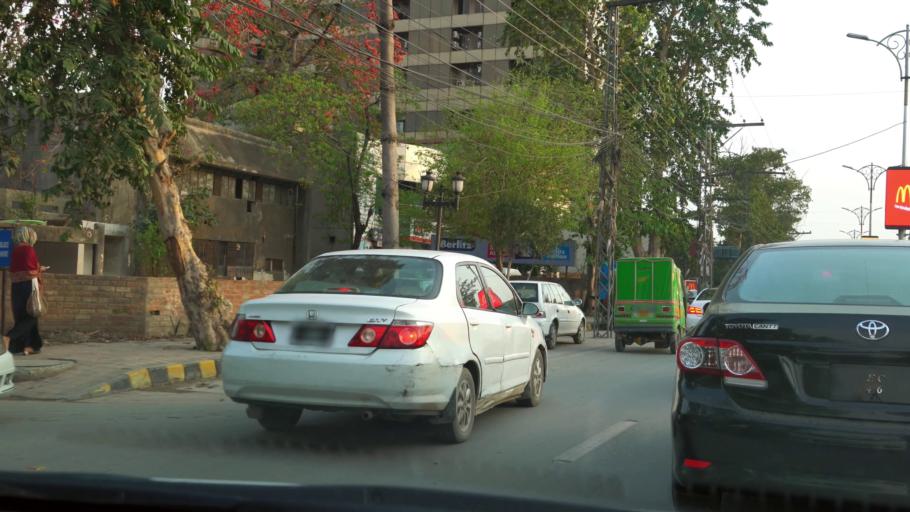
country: PK
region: Punjab
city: Lahore
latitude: 31.5122
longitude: 74.3510
